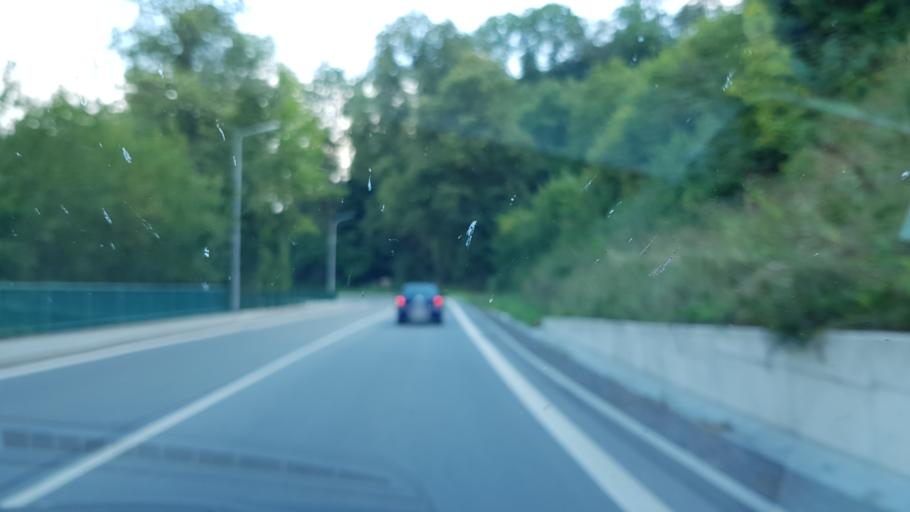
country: CZ
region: Pardubicky
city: Zamberk
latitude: 50.0879
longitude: 16.4581
